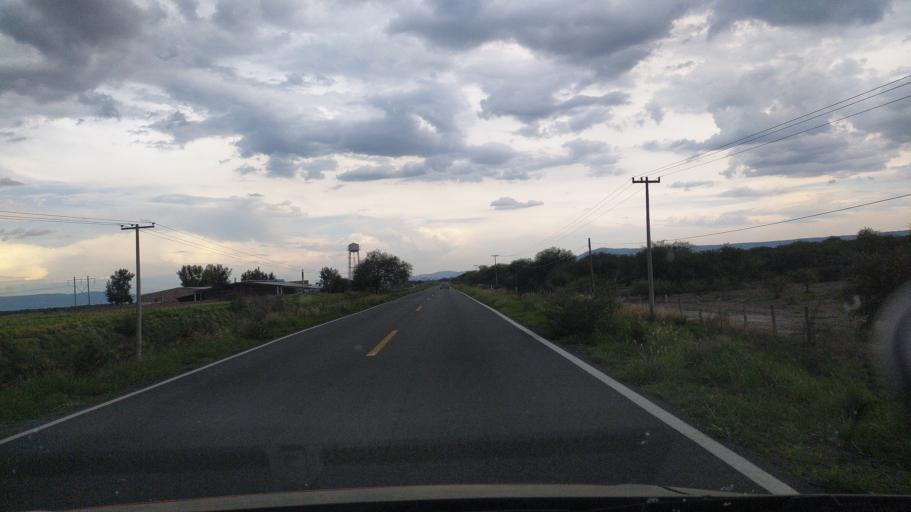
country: MX
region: Guanajuato
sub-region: San Francisco del Rincon
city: San Ignacio de Hidalgo
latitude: 20.8463
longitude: -101.8960
